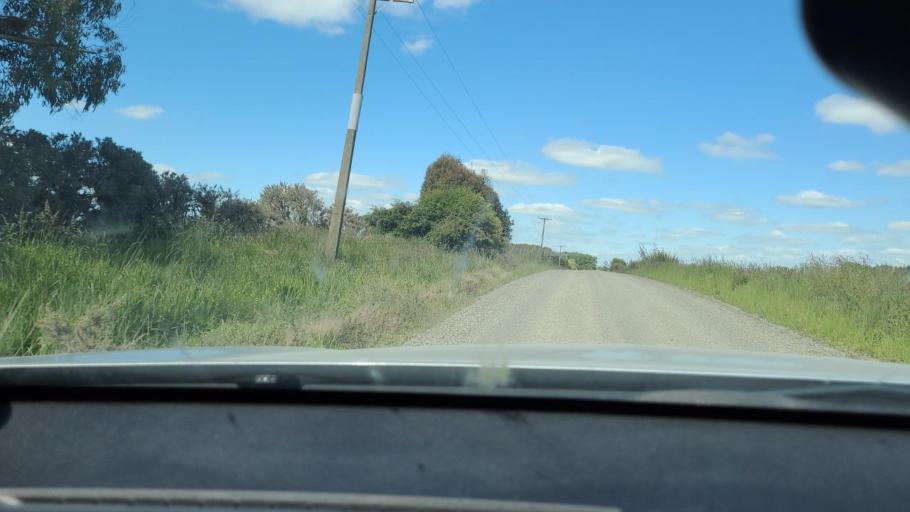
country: NZ
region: Southland
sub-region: Southland District
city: Riverton
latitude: -46.2412
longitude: 168.1338
